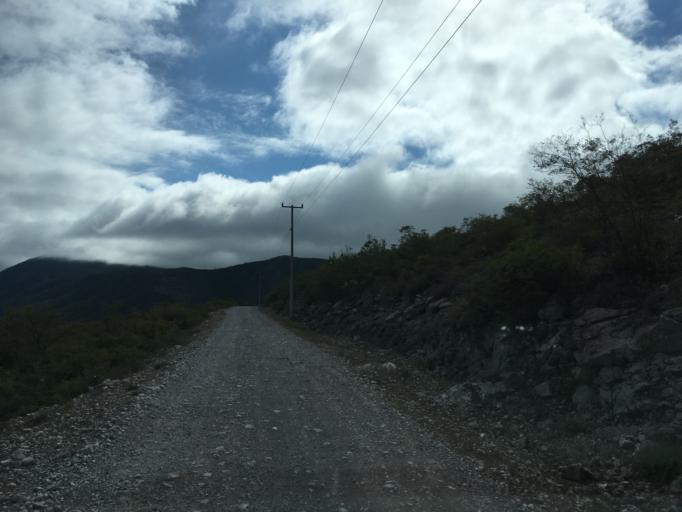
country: MX
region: Hidalgo
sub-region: Metztitlan
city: Fontezuelas
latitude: 20.6377
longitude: -98.8529
